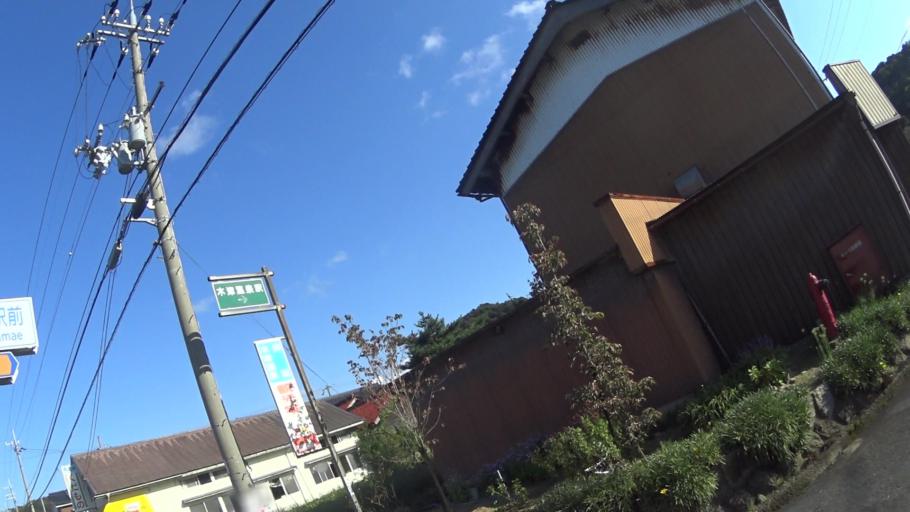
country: JP
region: Hyogo
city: Toyooka
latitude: 35.6511
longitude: 134.9727
